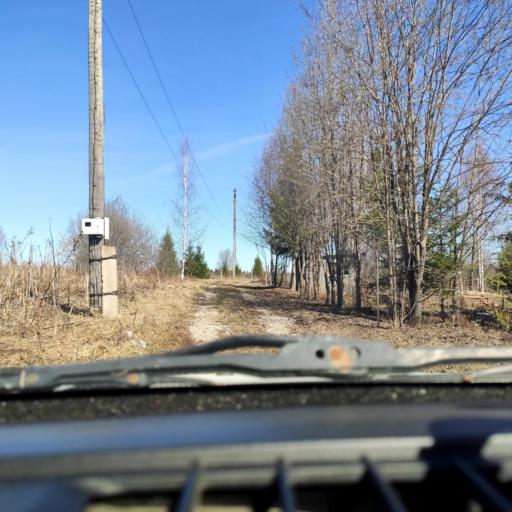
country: RU
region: Perm
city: Kultayevo
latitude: 57.8260
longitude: 55.7748
